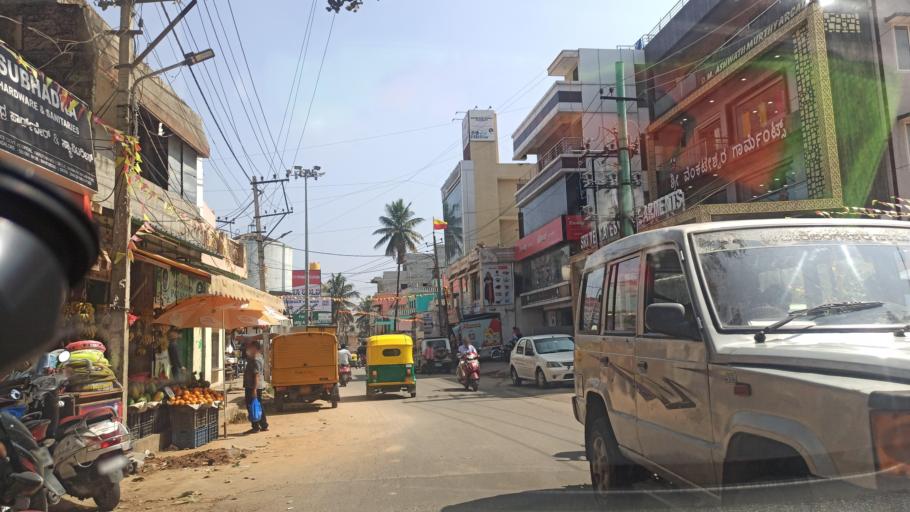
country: IN
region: Karnataka
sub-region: Bangalore Urban
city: Yelahanka
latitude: 13.0658
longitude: 77.6003
